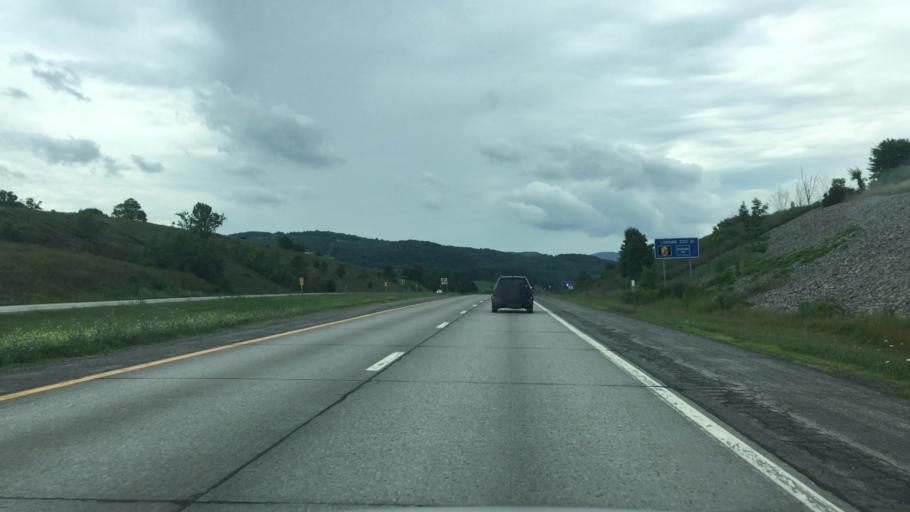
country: US
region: New York
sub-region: Schoharie County
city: Cobleskill
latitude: 42.6627
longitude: -74.4965
